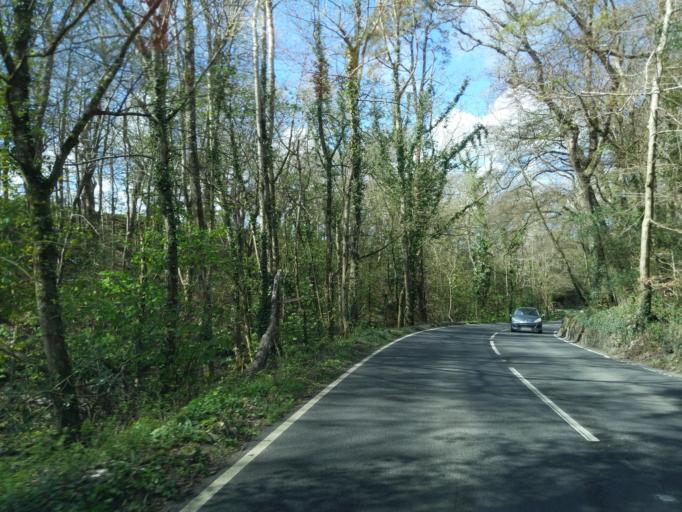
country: GB
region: England
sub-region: Cornwall
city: Helland
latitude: 50.5008
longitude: -4.7757
